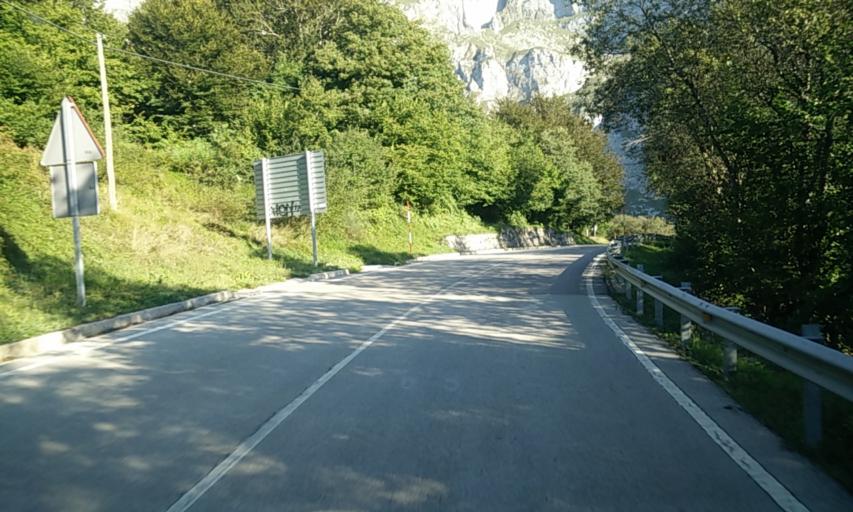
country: ES
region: Castille and Leon
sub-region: Provincia de Leon
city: Posada de Valdeon
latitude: 43.1412
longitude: -4.8100
